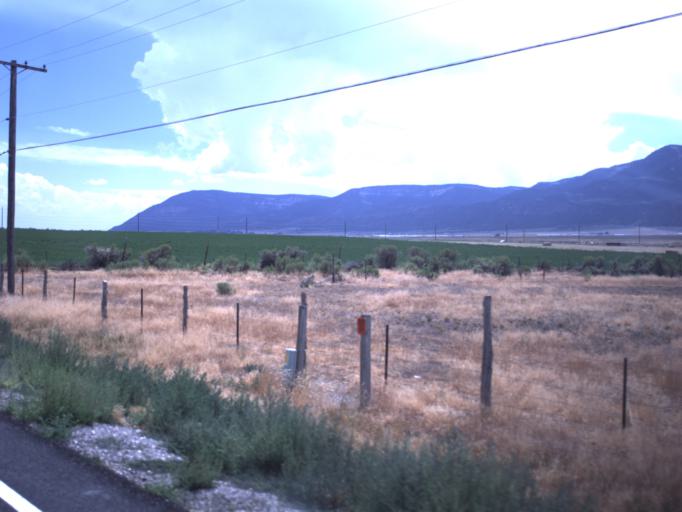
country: US
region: Utah
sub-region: Sanpete County
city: Moroni
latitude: 39.5558
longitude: -111.6006
